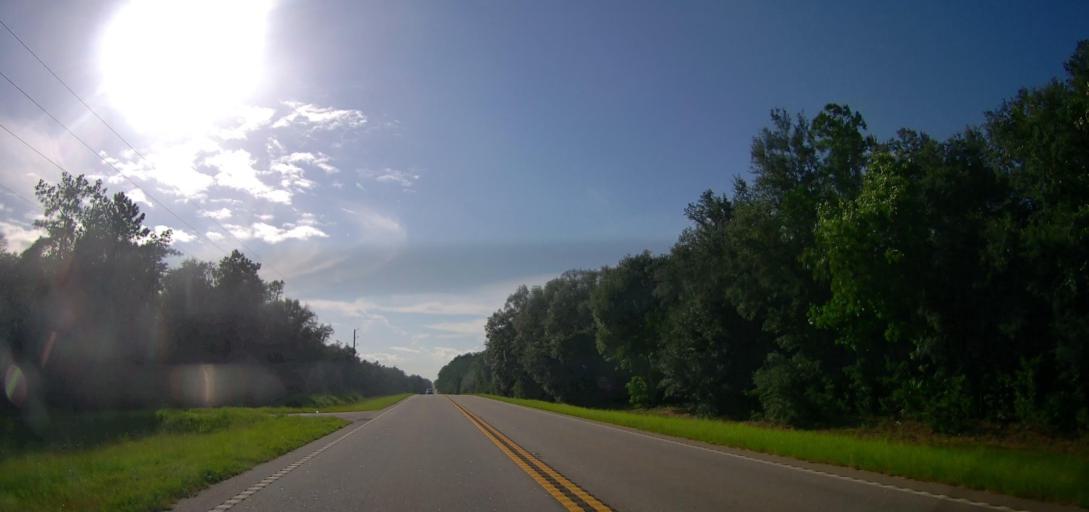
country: US
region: Georgia
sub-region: Coffee County
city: Douglas
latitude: 31.4632
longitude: -82.7538
